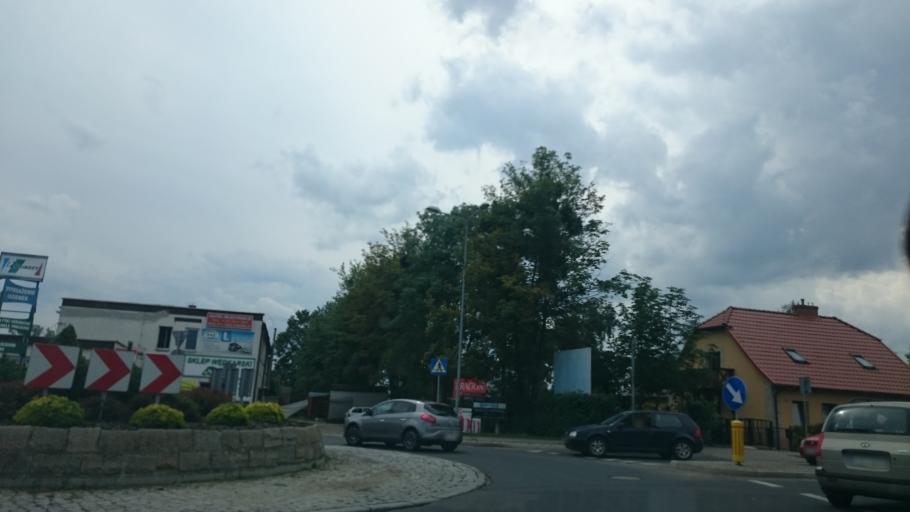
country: PL
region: Kujawsko-Pomorskie
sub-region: Powiat tucholski
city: Tuchola
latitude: 53.5815
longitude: 17.8713
